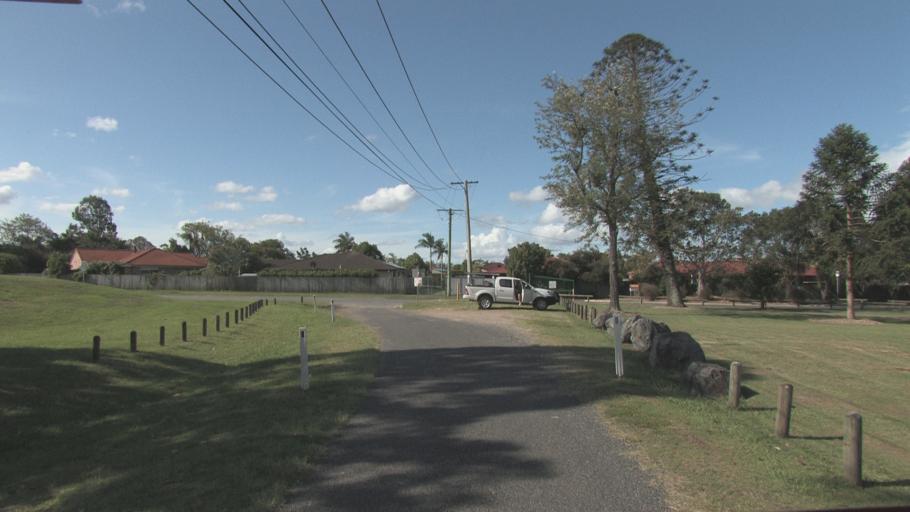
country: AU
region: Queensland
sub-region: Logan
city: Slacks Creek
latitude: -27.6732
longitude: 153.1511
